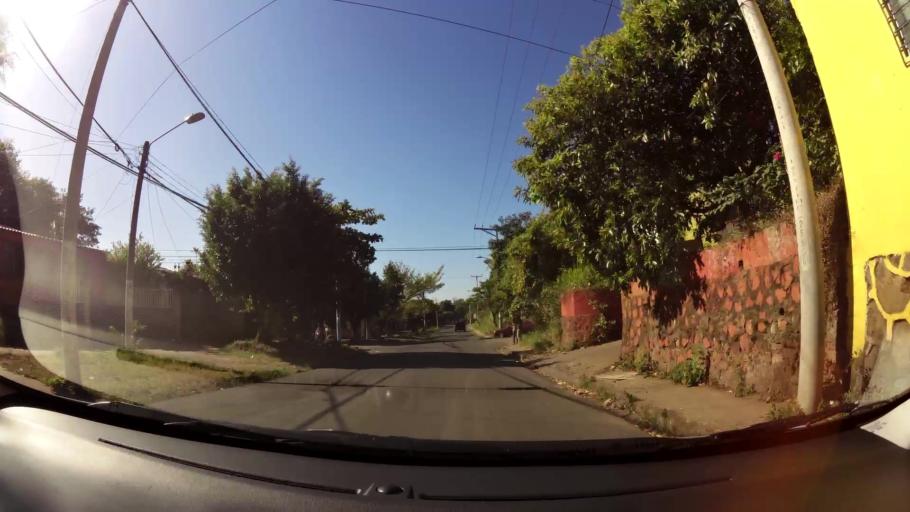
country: SV
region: Sonsonate
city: Sonzacate
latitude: 13.7317
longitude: -89.7199
